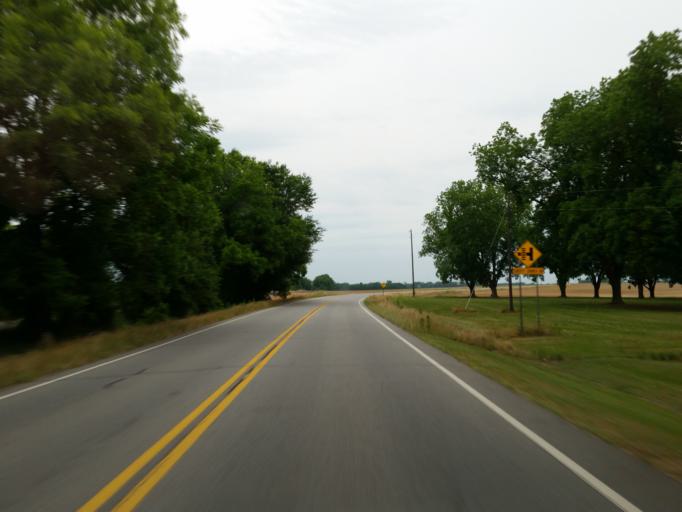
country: US
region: Georgia
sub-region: Dooly County
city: Vienna
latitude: 32.1744
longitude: -83.7659
